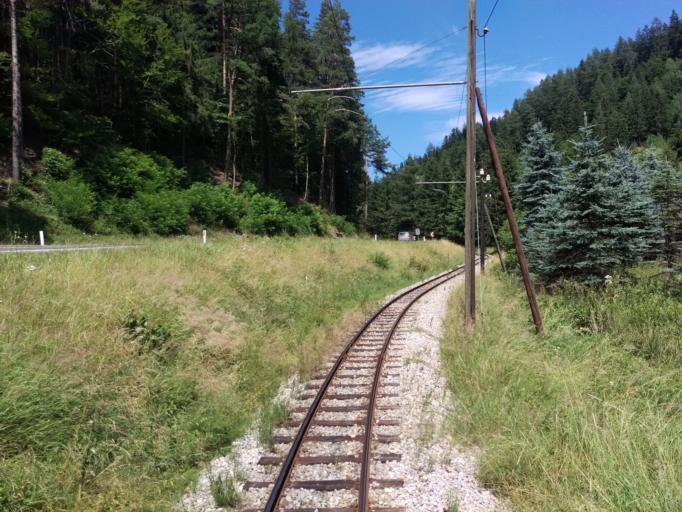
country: AT
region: Styria
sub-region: Politischer Bezirk Bruck-Muerzzuschlag
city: Pernegg an der Mur
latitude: 47.3505
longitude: 15.3653
